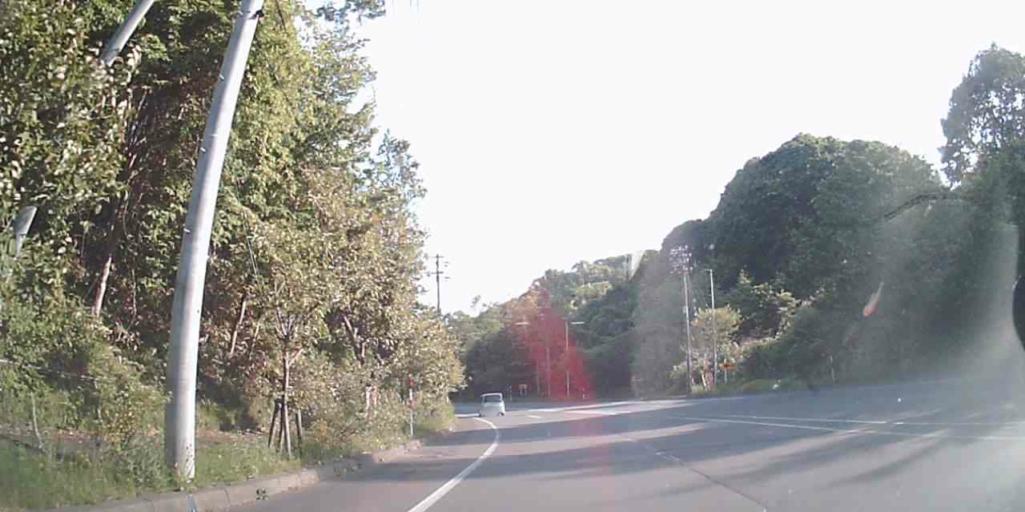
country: JP
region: Hokkaido
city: Shiraoi
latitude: 42.4629
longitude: 141.1774
